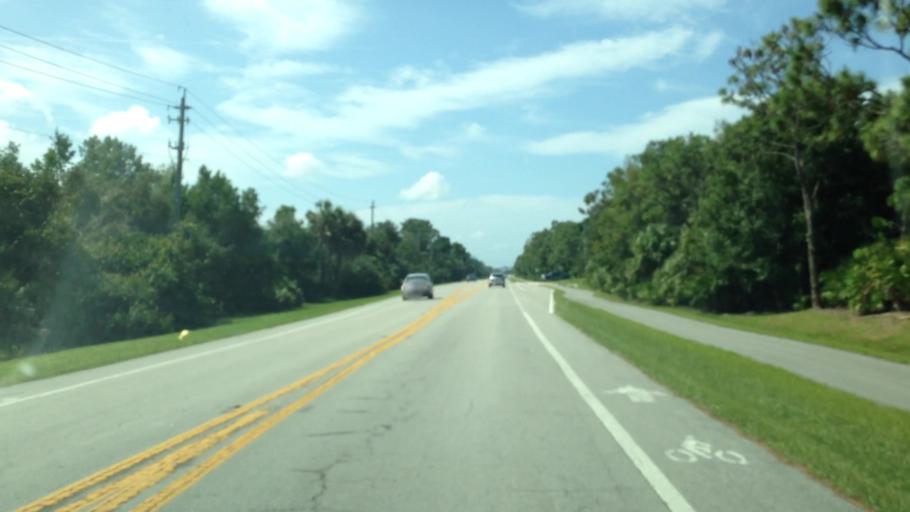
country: US
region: Florida
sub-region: Lee County
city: Bonita Springs
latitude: 26.3115
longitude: -81.8189
